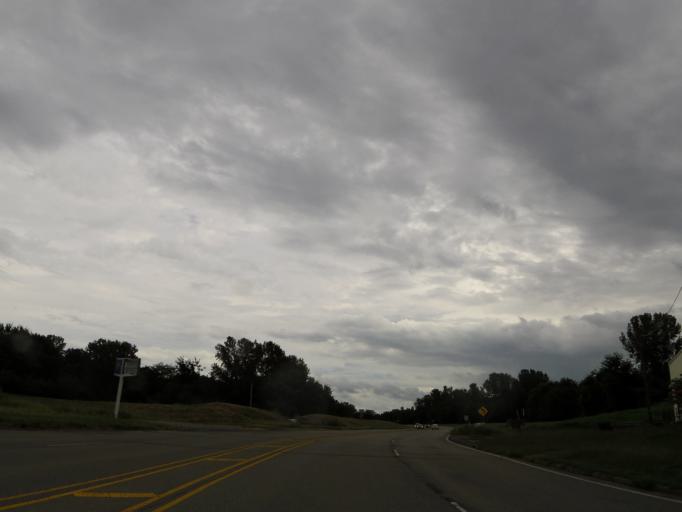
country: US
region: Illinois
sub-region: Alexander County
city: Cairo
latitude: 36.9966
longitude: -89.1622
